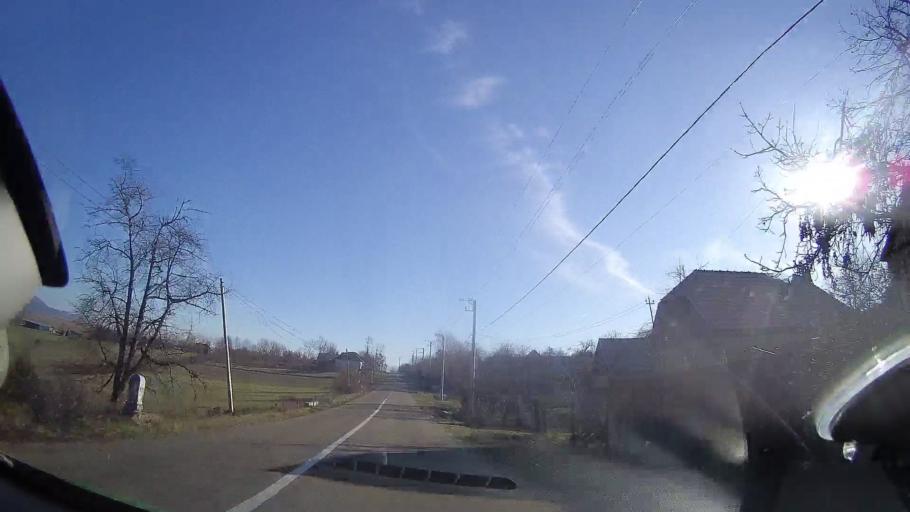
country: RO
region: Bihor
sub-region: Comuna Vadu Crisului
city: Vadu Crisului
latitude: 46.9756
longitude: 22.5370
